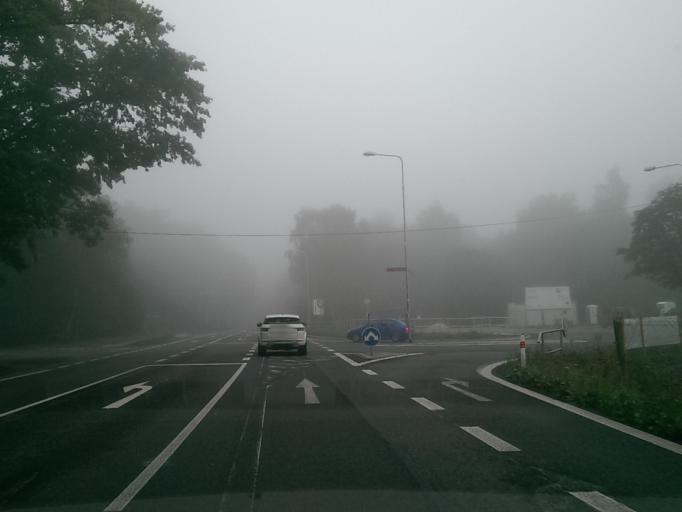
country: CZ
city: Doksy
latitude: 50.5849
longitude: 14.6293
